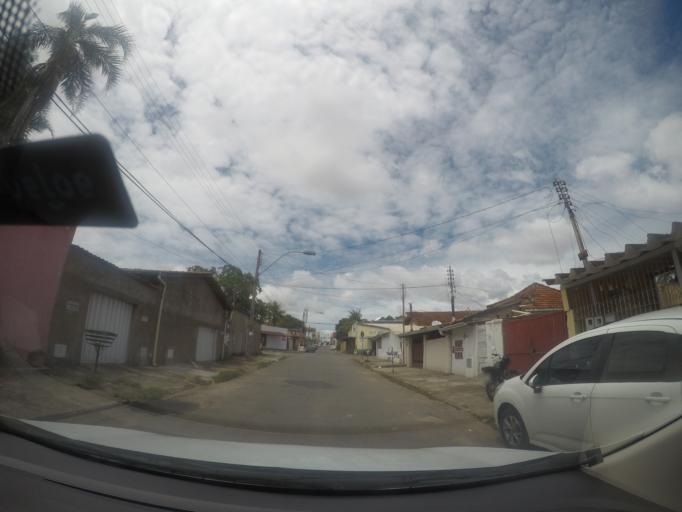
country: BR
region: Goias
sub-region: Goiania
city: Goiania
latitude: -16.6649
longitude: -49.2850
